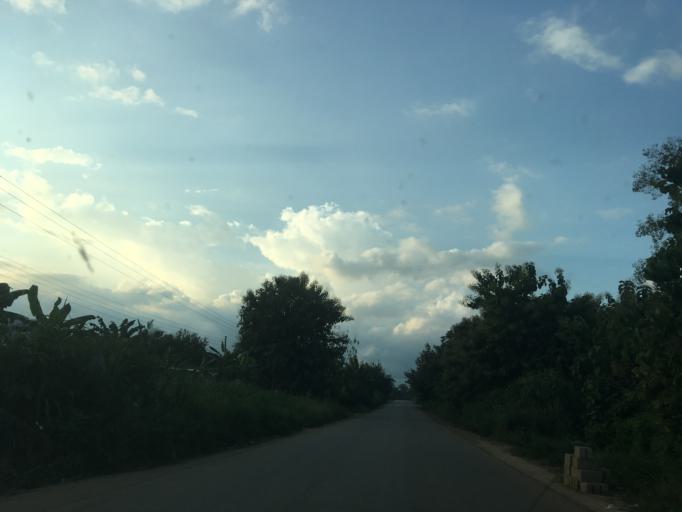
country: GH
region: Western
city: Bibiani
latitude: 6.6536
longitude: -2.4259
